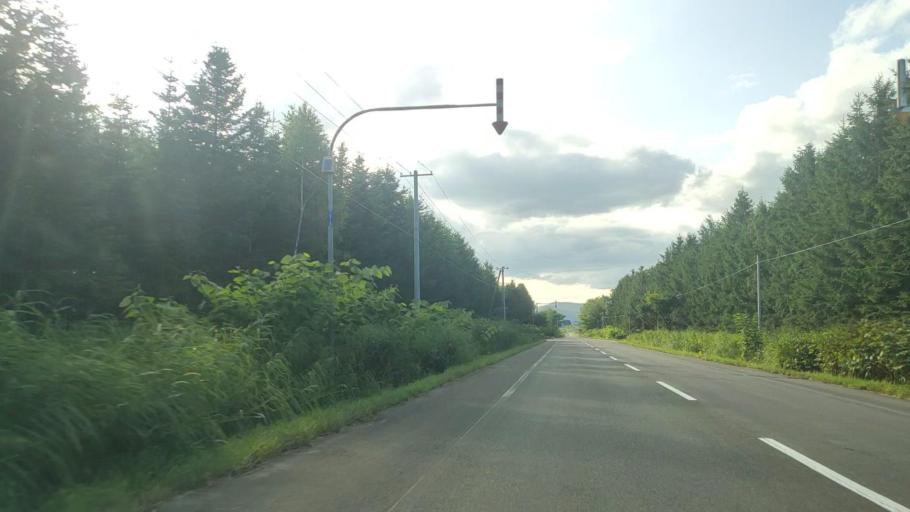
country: JP
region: Hokkaido
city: Makubetsu
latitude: 44.8889
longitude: 142.0041
